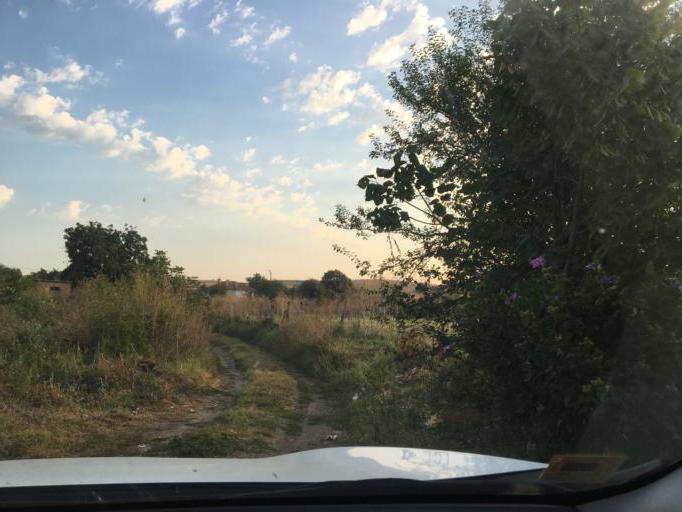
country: BG
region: Burgas
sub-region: Obshtina Burgas
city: Burgas
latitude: 42.6124
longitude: 27.4969
